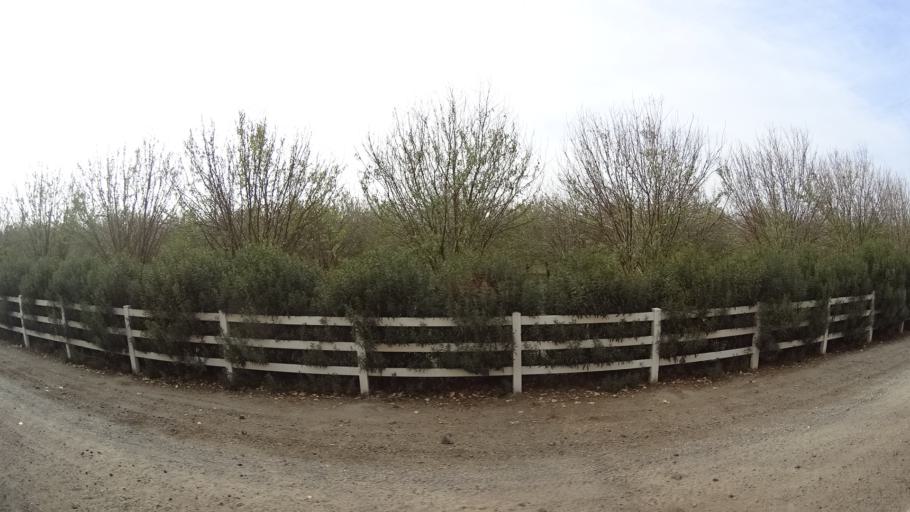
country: US
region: California
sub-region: Kern County
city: Greenacres
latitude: 35.2907
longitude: -119.1281
